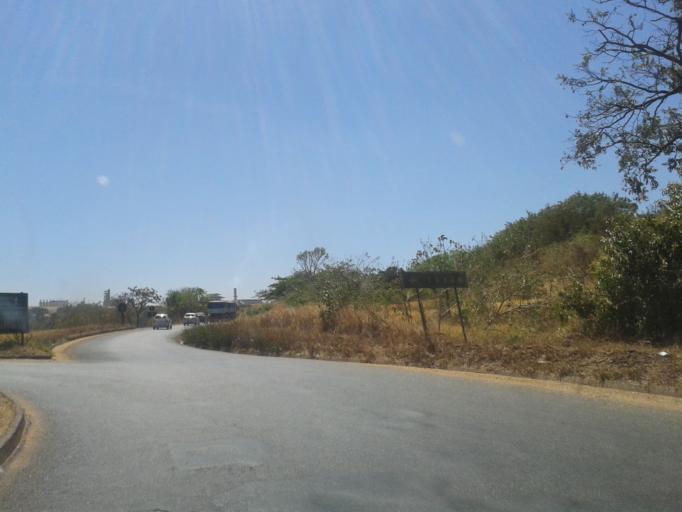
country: BR
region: Minas Gerais
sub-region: Uberlandia
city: Uberlandia
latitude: -18.8604
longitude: -48.2936
